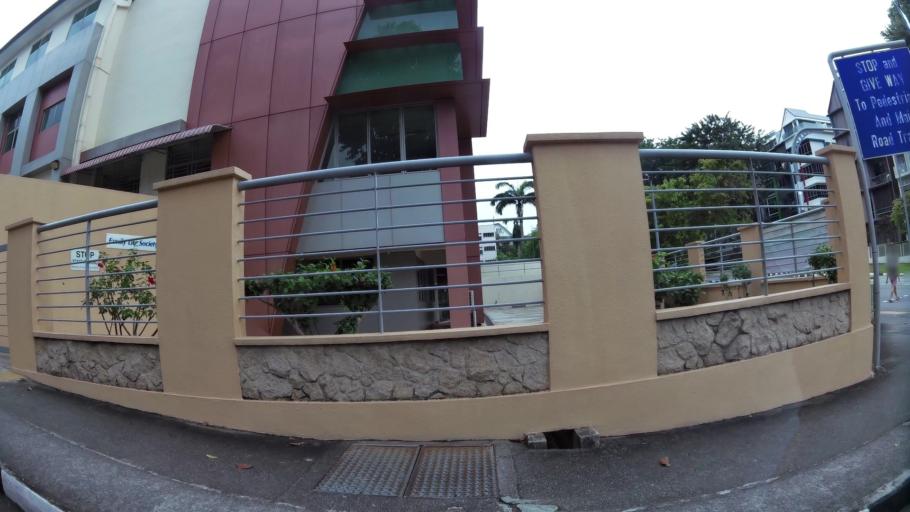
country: SG
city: Singapore
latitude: 1.3557
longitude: 103.8768
